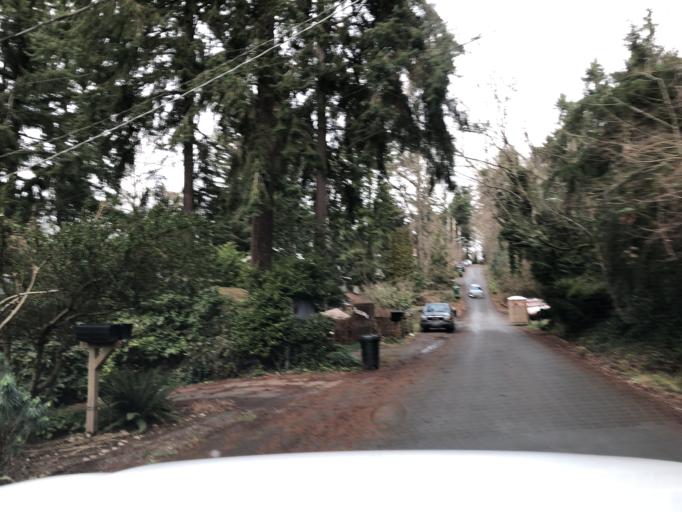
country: US
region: Washington
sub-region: King County
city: Inglewood-Finn Hill
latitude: 47.7021
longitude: -122.2789
